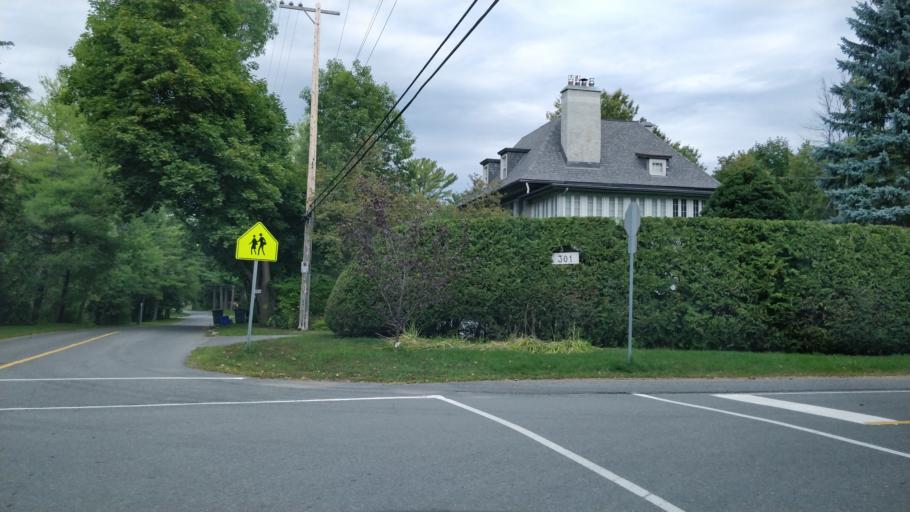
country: CA
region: Quebec
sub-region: Outaouais
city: Gatineau
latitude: 45.4509
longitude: -75.6791
